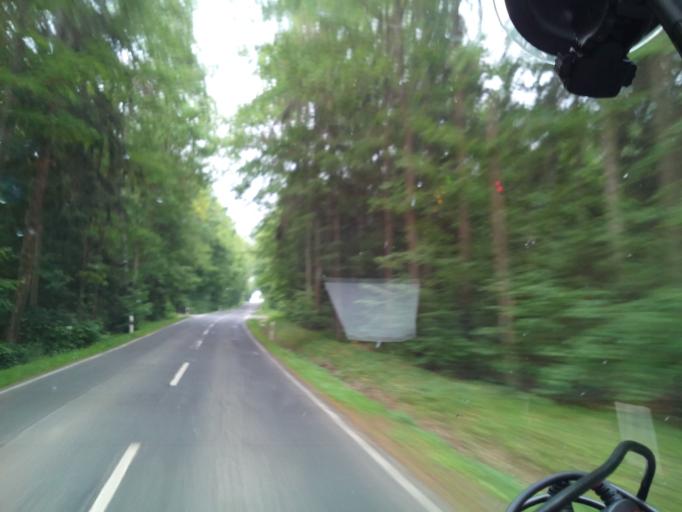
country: DE
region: Bavaria
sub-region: Regierungsbezirk Unterfranken
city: Hendungen
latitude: 50.3974
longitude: 10.3835
